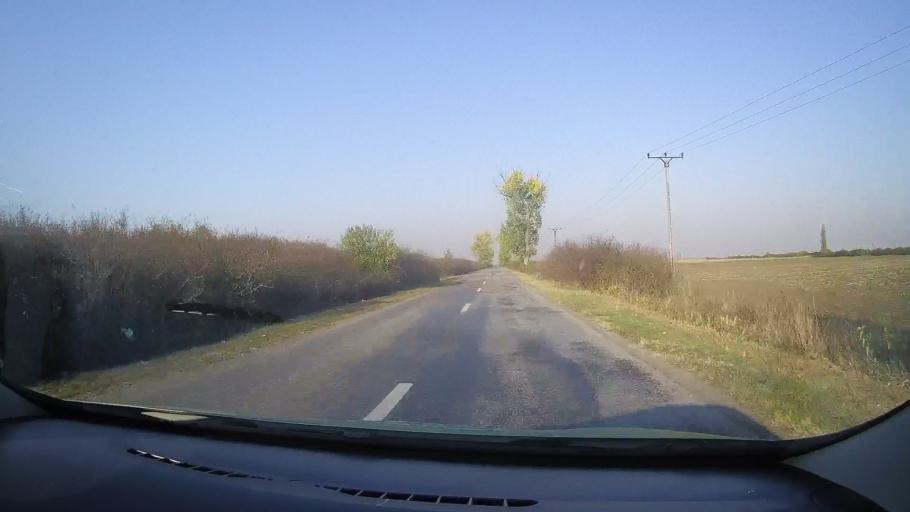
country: RO
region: Arad
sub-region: Comuna Socodor
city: Socodor
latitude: 46.5028
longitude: 21.4179
